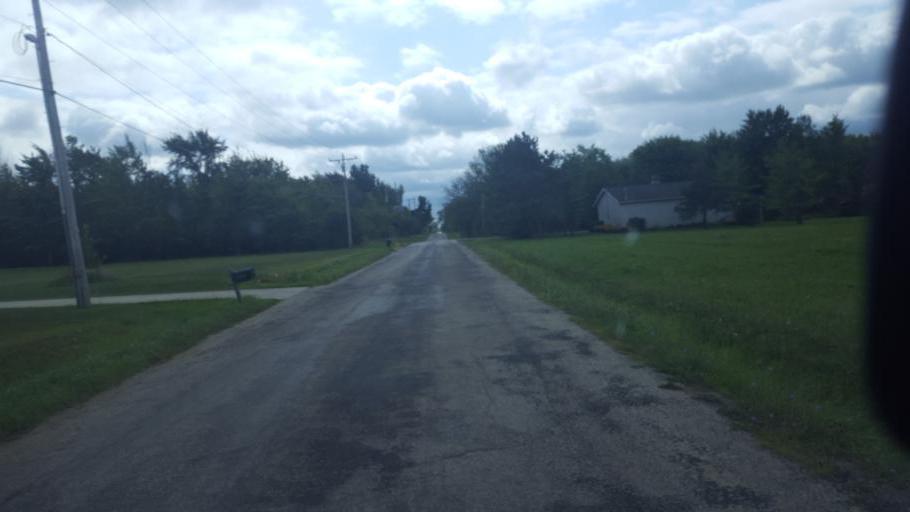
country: US
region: Ohio
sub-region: Geauga County
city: Chardon
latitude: 41.6565
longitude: -81.1127
